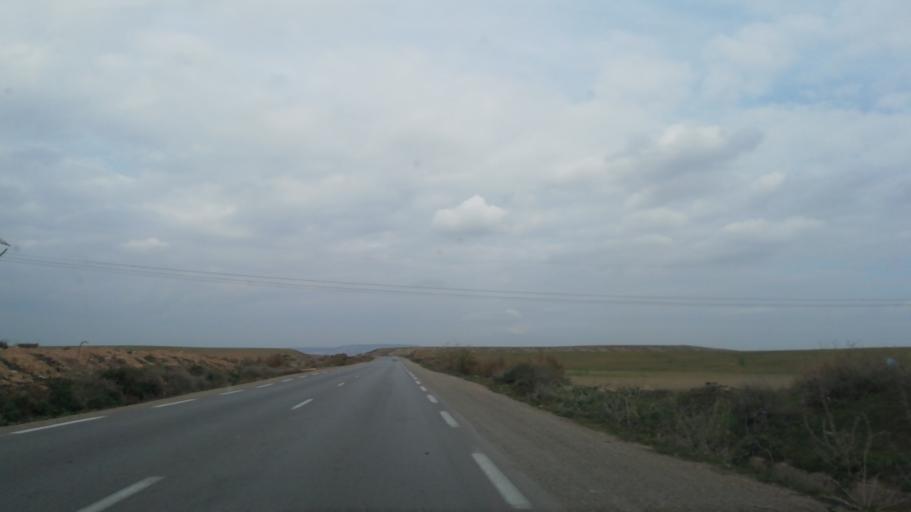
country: DZ
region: Mostaganem
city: Mostaganem
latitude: 35.7123
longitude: 0.0548
